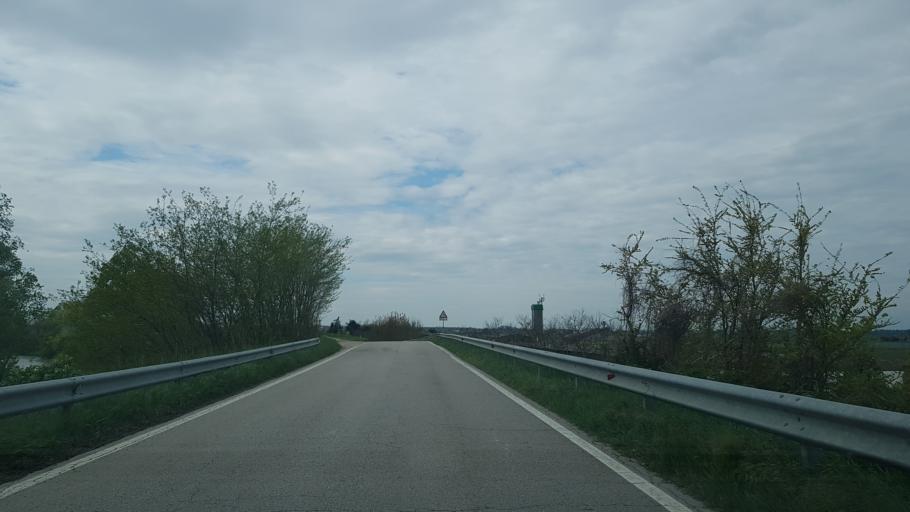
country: IT
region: Veneto
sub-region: Provincia di Padova
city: Piacenza d'Adige
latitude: 45.1250
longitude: 11.5772
